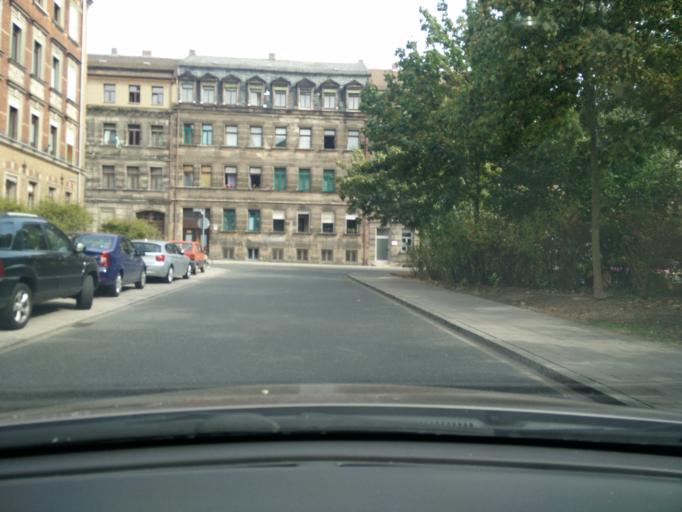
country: DE
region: Bavaria
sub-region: Regierungsbezirk Mittelfranken
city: Furth
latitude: 49.4751
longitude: 10.9813
